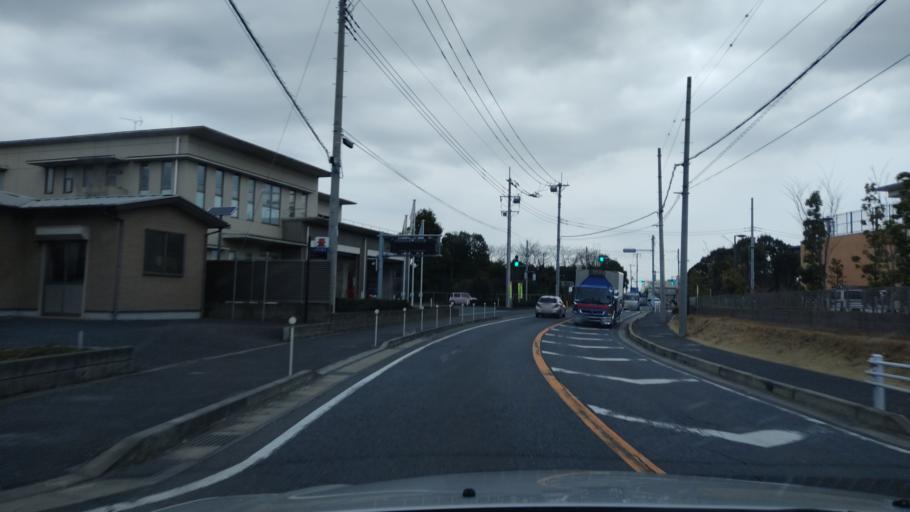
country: JP
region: Ibaraki
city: Moriya
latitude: 35.9138
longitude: 139.9471
